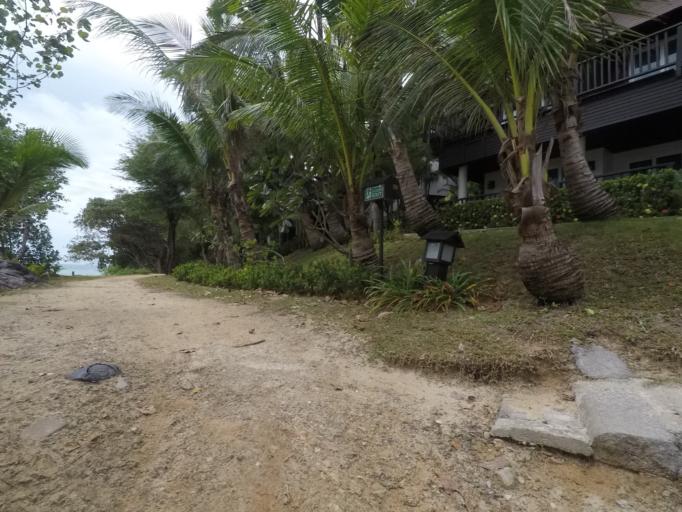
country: TH
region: Phangnga
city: Ban Phru Nai
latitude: 7.7735
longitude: 98.7657
